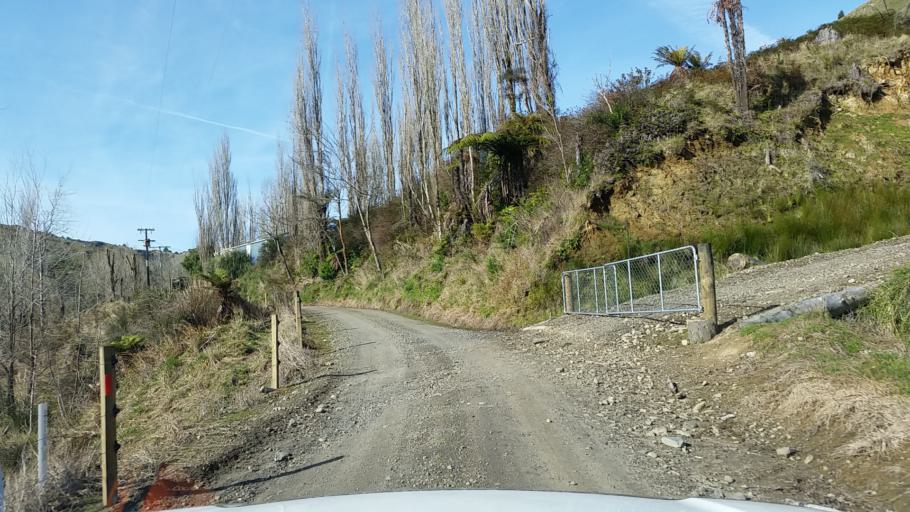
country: NZ
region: Taranaki
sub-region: South Taranaki District
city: Eltham
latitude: -39.3653
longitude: 174.5174
